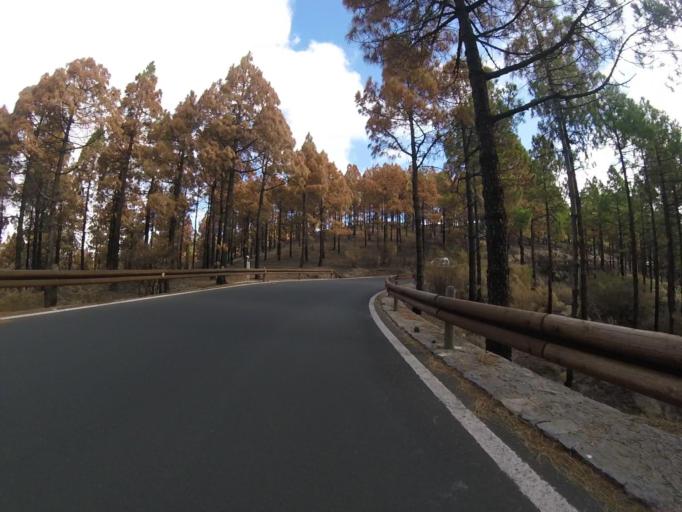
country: ES
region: Canary Islands
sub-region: Provincia de Las Palmas
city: Tejeda
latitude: 27.9739
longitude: -15.5776
